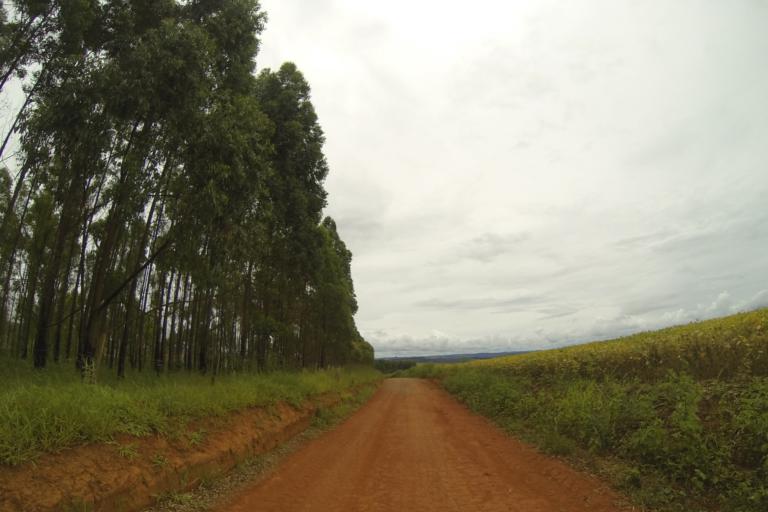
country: BR
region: Minas Gerais
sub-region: Ibia
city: Ibia
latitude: -19.7425
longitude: -46.6342
